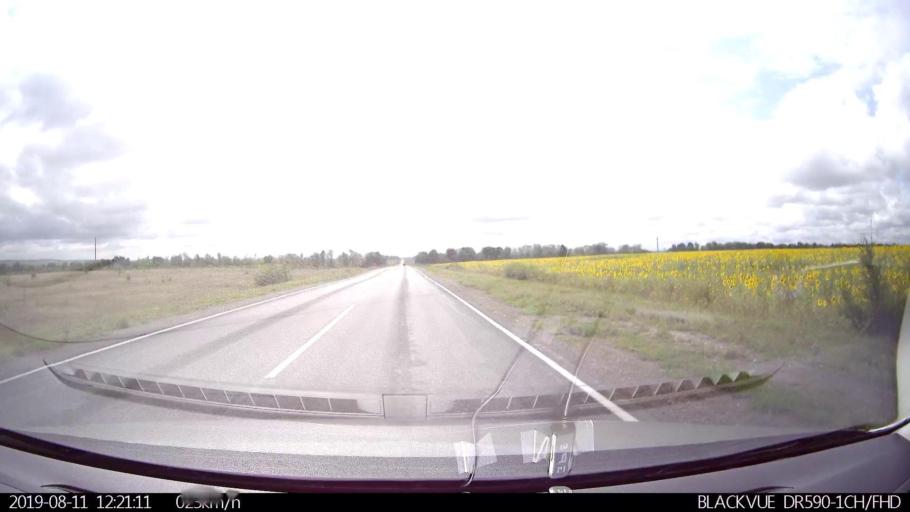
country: RU
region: Ulyanovsk
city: Ignatovka
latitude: 53.9227
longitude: 47.9577
